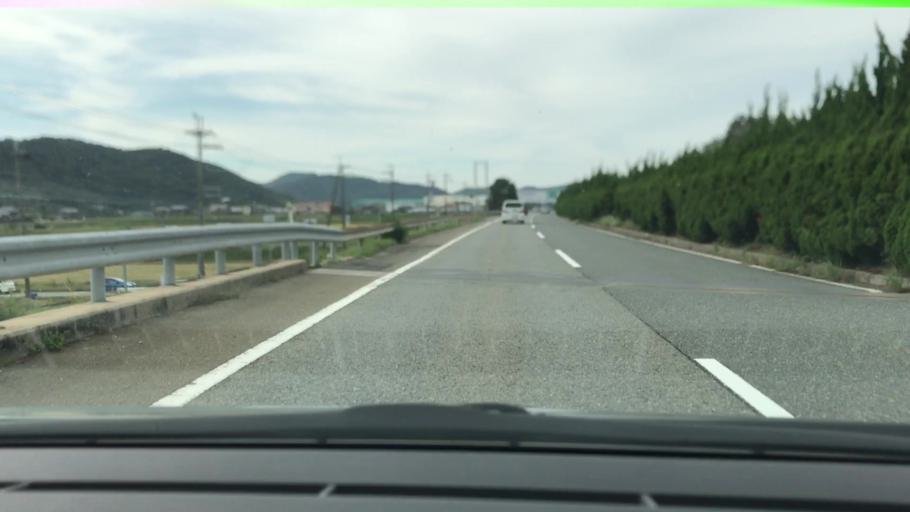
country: JP
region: Hyogo
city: Himeji
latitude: 34.8999
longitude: 134.7513
